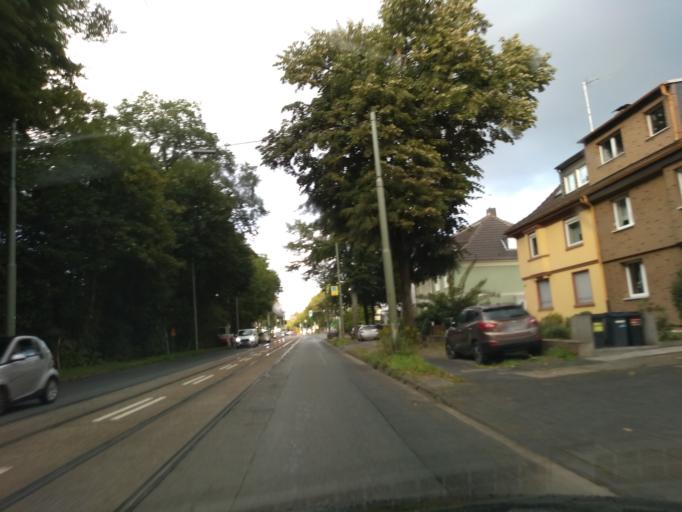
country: DE
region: North Rhine-Westphalia
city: Hattingen
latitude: 51.4413
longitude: 7.1897
